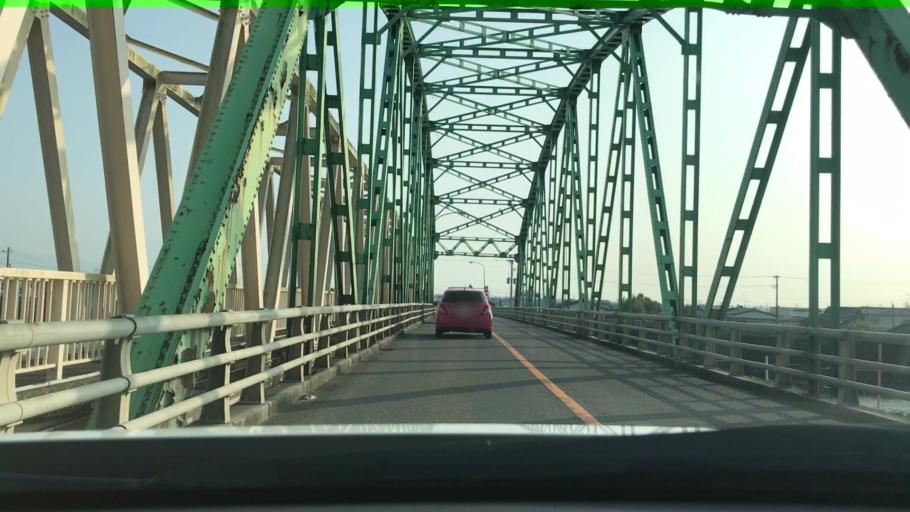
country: JP
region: Saga Prefecture
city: Saga-shi
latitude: 33.2002
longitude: 130.1959
